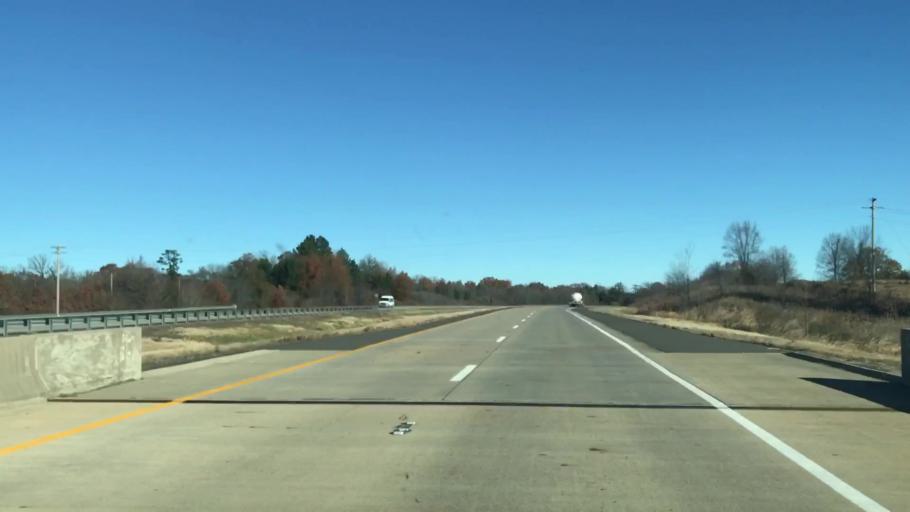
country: US
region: Texas
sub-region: Cass County
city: Queen City
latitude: 33.1536
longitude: -93.8898
